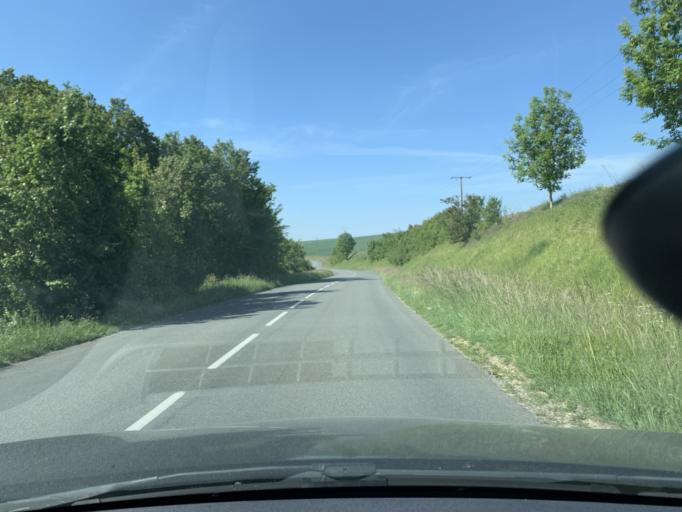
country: FR
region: Nord-Pas-de-Calais
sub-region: Departement du Nord
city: Masnieres
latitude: 50.0867
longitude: 3.2225
